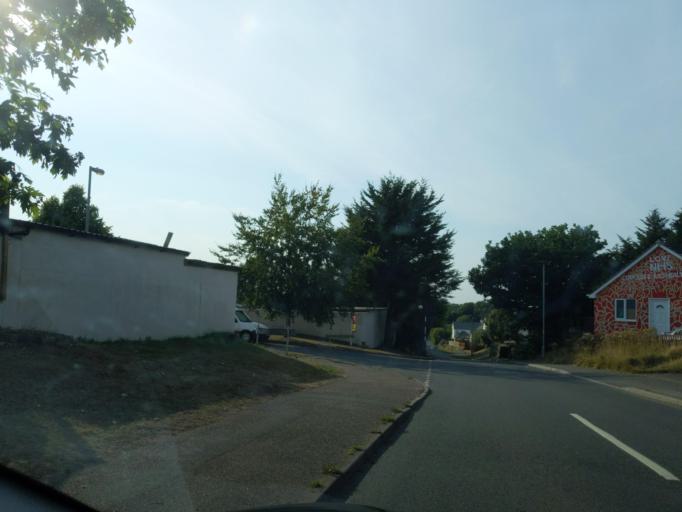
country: GB
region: England
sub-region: Devon
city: Winkleigh
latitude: 50.9690
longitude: -3.9970
